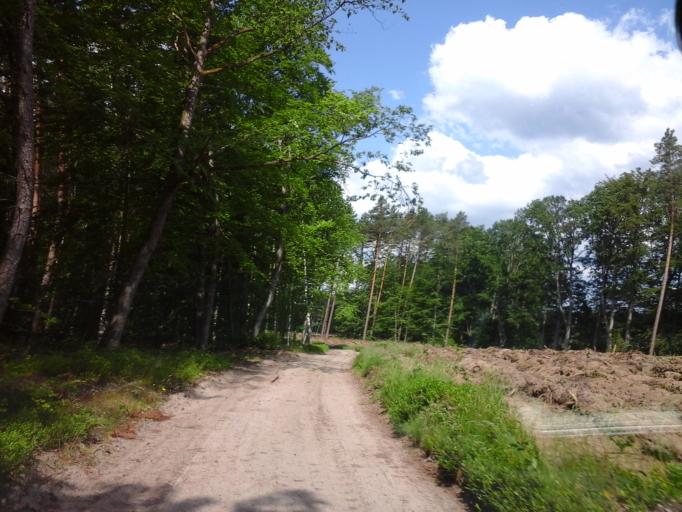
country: PL
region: West Pomeranian Voivodeship
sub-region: Powiat choszczenski
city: Bierzwnik
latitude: 53.0880
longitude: 15.7597
